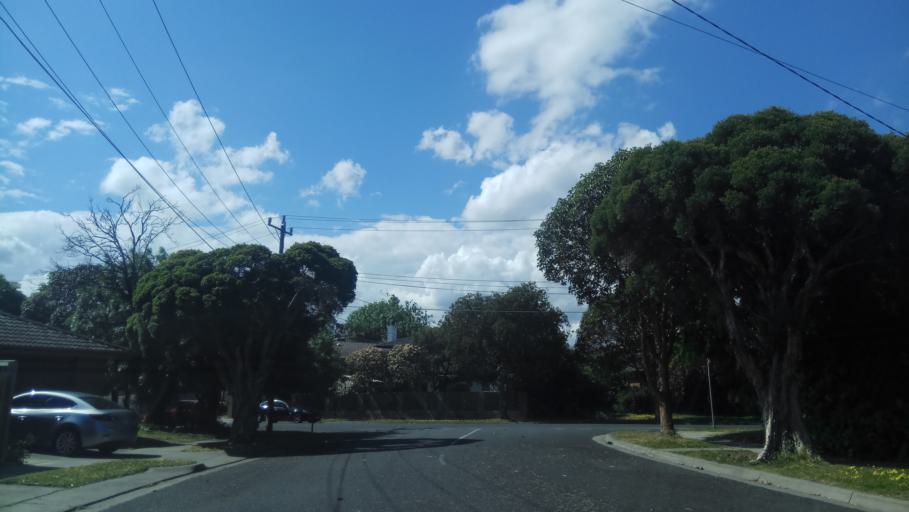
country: AU
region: Victoria
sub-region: Kingston
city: Dingley Village
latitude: -37.9825
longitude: 145.1186
